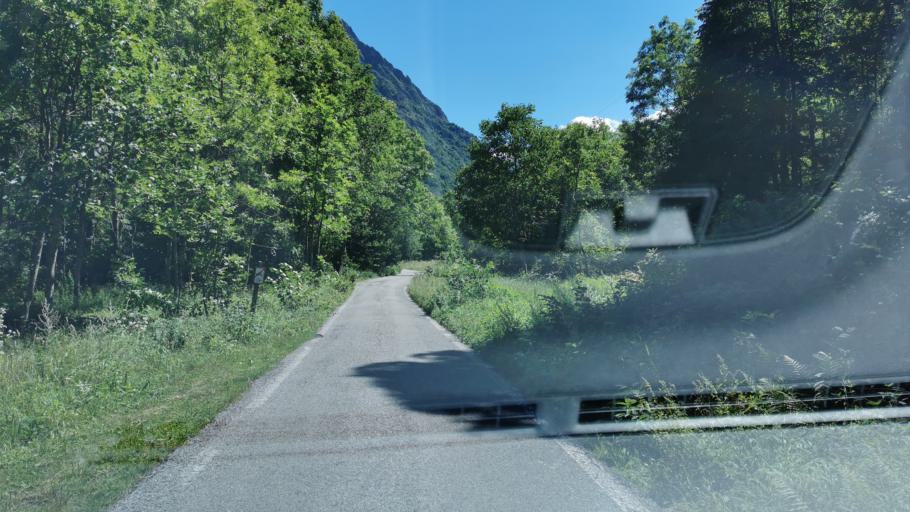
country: IT
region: Piedmont
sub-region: Provincia di Cuneo
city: Entracque
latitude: 44.2041
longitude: 7.3802
